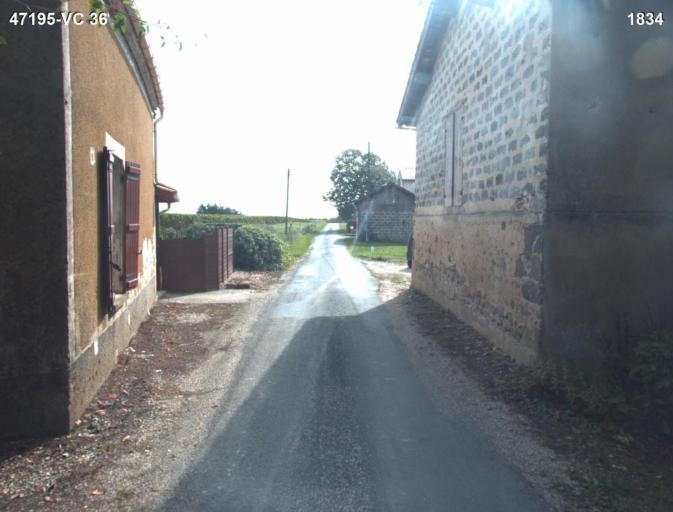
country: FR
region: Aquitaine
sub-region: Departement du Lot-et-Garonne
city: Nerac
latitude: 44.1244
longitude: 0.3275
